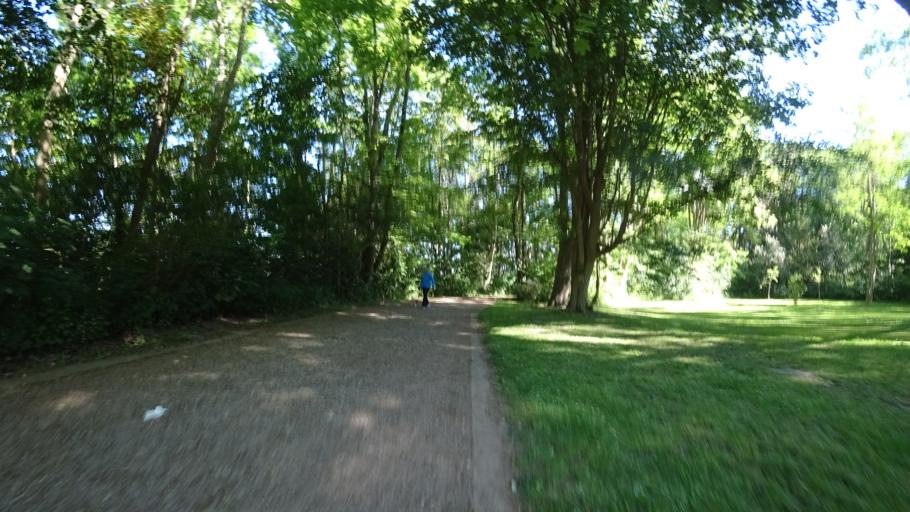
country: DE
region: North Rhine-Westphalia
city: Erwitte
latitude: 51.6348
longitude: 8.3532
